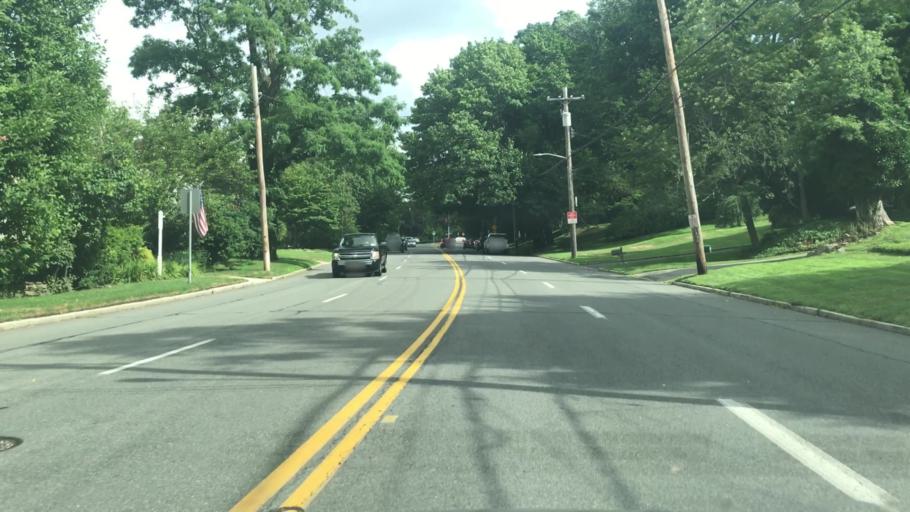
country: US
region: New York
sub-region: Westchester County
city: Tuckahoe
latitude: 40.9525
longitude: -73.7962
